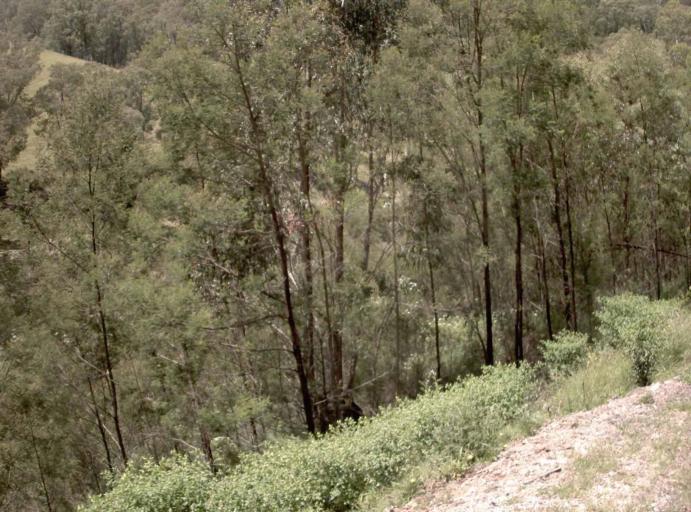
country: AU
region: Victoria
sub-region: East Gippsland
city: Lakes Entrance
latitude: -37.5190
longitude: 147.8486
